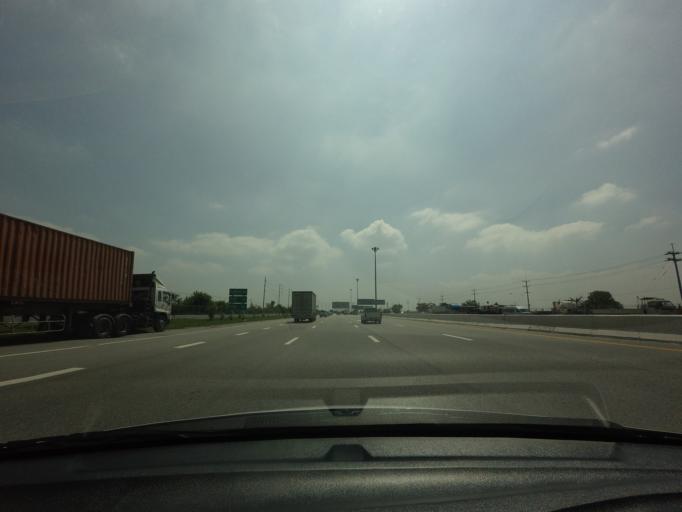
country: TH
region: Chachoengsao
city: Bang Pakong
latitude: 13.5959
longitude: 100.9595
